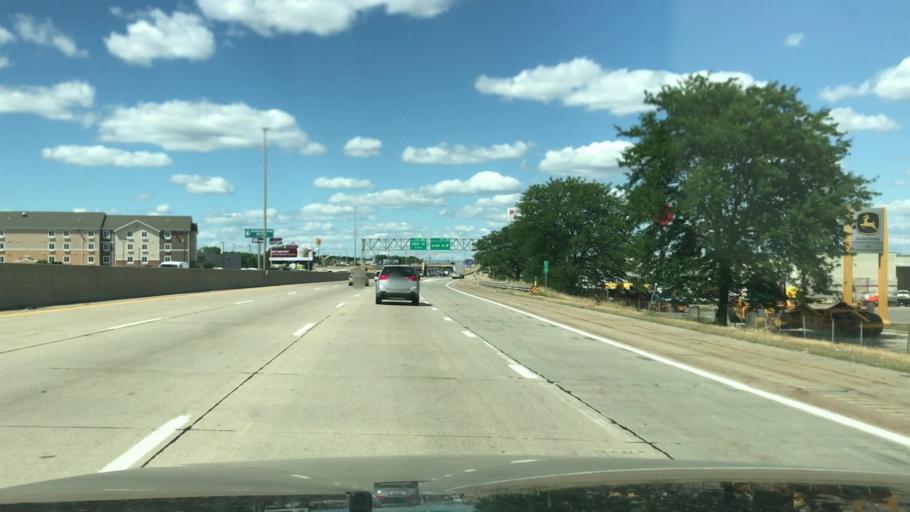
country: US
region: Michigan
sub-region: Kent County
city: Kentwood
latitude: 42.8798
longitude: -85.6818
